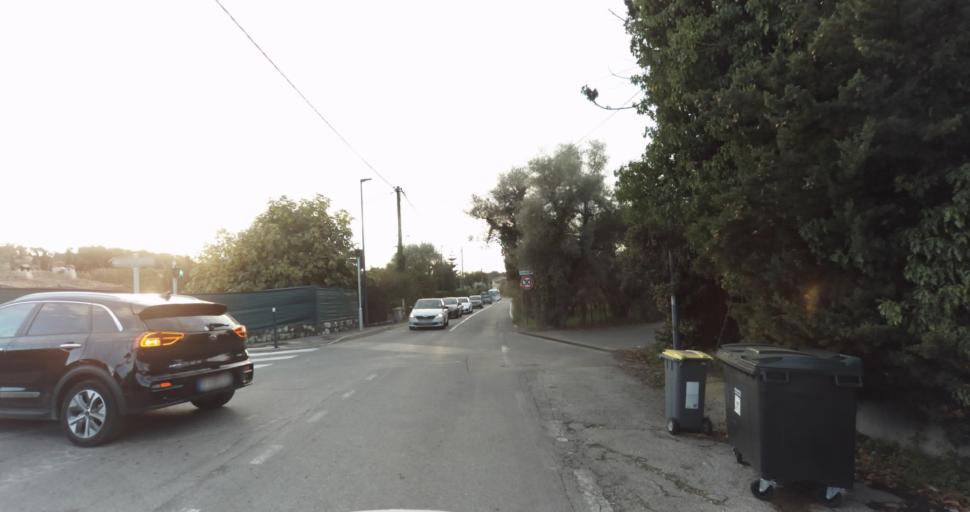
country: FR
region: Provence-Alpes-Cote d'Azur
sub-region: Departement des Alpes-Maritimes
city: Saint-Paul-de-Vence
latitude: 43.7129
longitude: 7.1290
